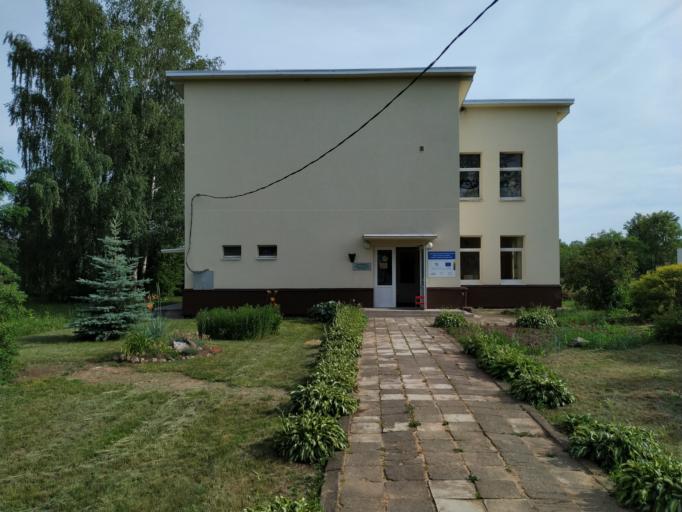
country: LT
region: Panevezys
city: Pasvalys
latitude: 56.1285
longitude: 24.4748
